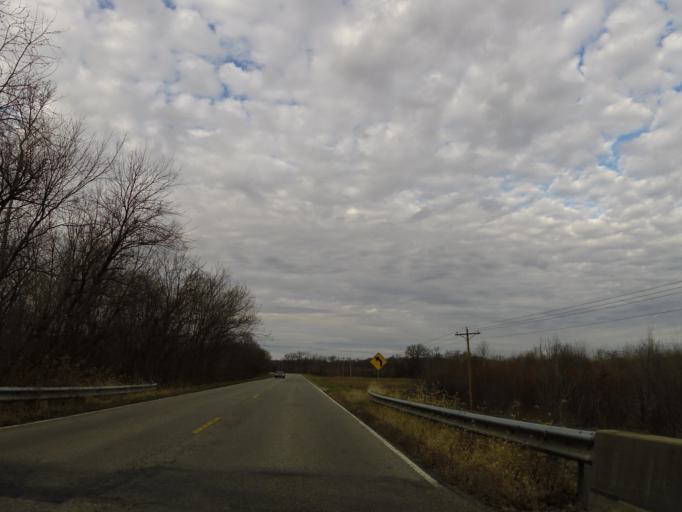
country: US
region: Illinois
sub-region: Jefferson County
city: Mount Vernon
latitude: 38.3783
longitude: -89.0226
